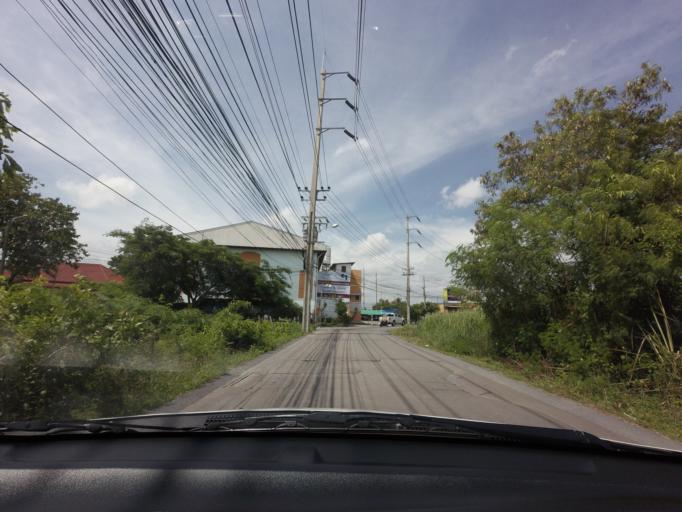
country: TH
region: Bangkok
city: Bang Na
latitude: 13.6149
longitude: 100.6740
